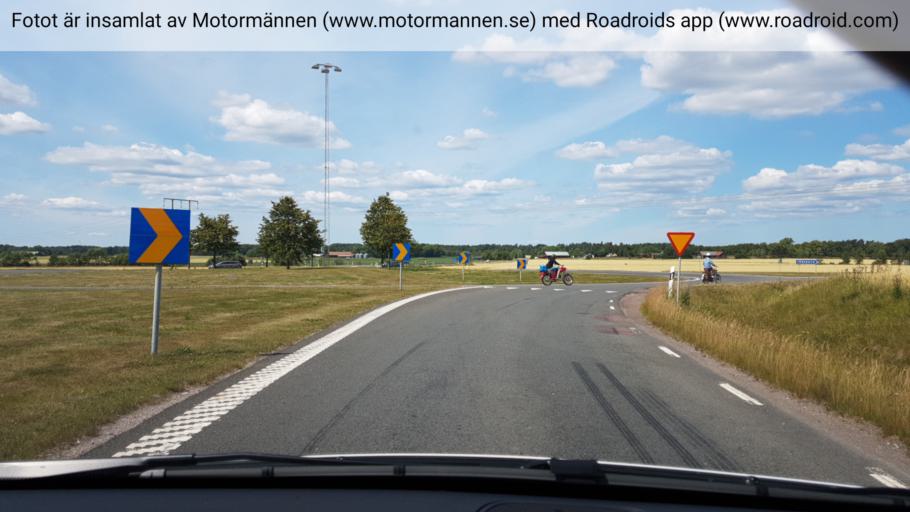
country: SE
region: Vaestra Goetaland
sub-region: Toreboda Kommun
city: Toereboda
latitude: 58.6084
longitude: 14.0111
